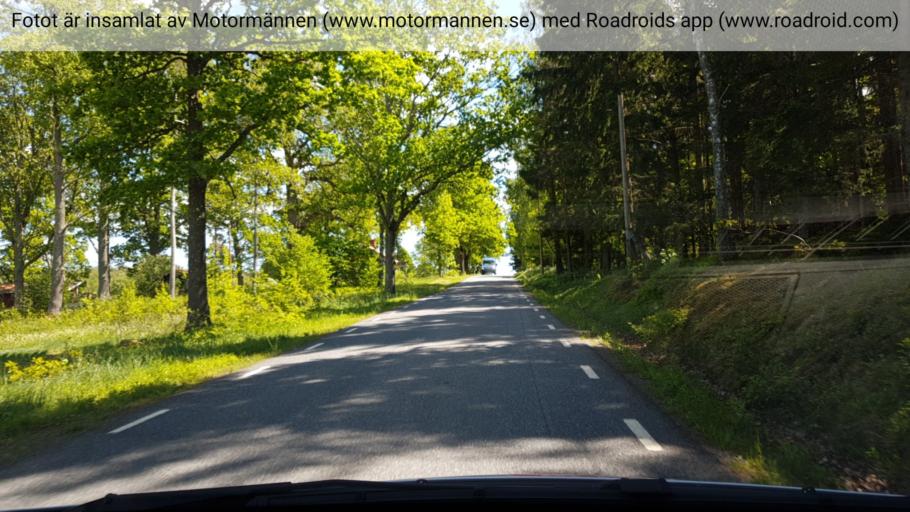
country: SE
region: Kalmar
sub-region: Vasterviks Kommun
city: Forserum
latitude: 57.9681
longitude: 16.6212
